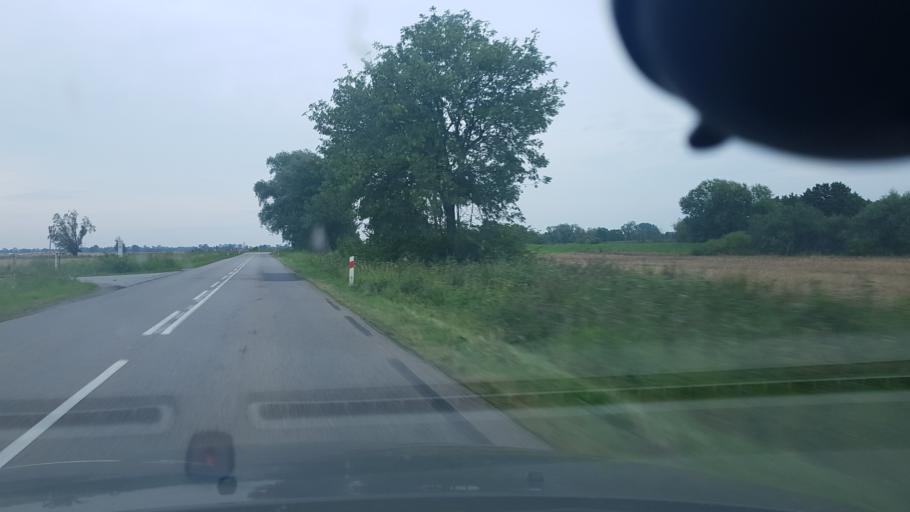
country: PL
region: Pomeranian Voivodeship
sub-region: Powiat nowodworski
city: Nowy Dwor Gdanski
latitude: 54.2363
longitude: 19.1280
